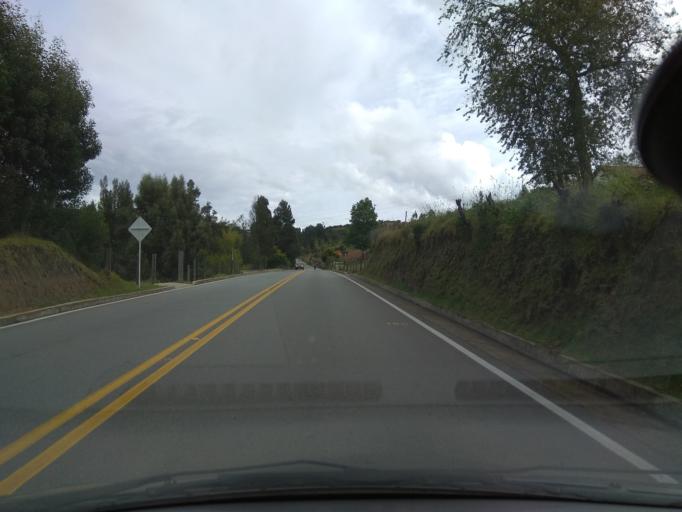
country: CO
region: Boyaca
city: Santa Rosa de Viterbo
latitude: 5.8911
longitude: -72.9781
